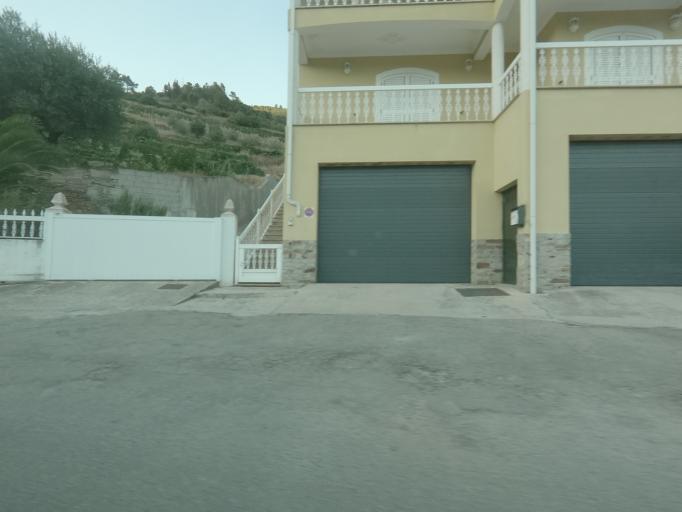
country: PT
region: Viseu
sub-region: Armamar
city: Armamar
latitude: 41.1595
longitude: -7.6825
